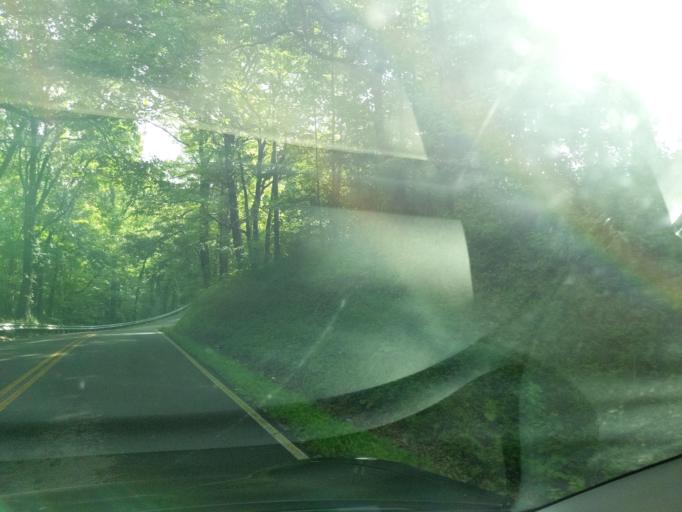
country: US
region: Ohio
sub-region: Fairfield County
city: Lancaster
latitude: 39.5581
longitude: -82.6173
